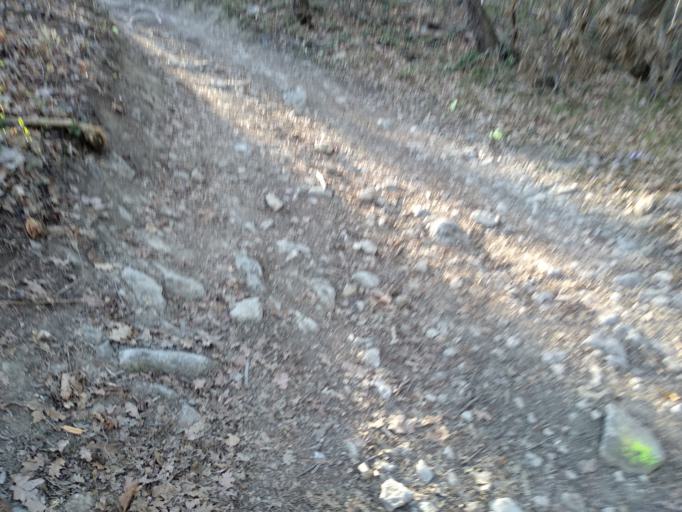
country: IT
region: Emilia-Romagna
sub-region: Provincia di Reggio Emilia
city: Castelnovo ne'Monti
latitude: 44.4199
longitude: 10.4175
